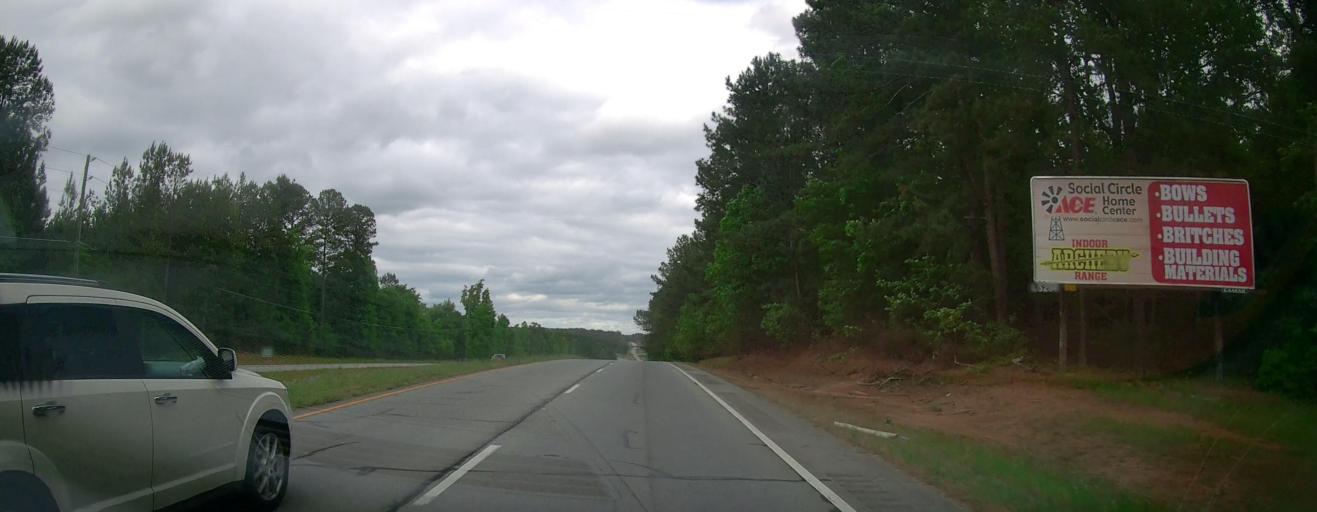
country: US
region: Georgia
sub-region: Walton County
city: Monroe
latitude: 33.8065
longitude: -83.7681
